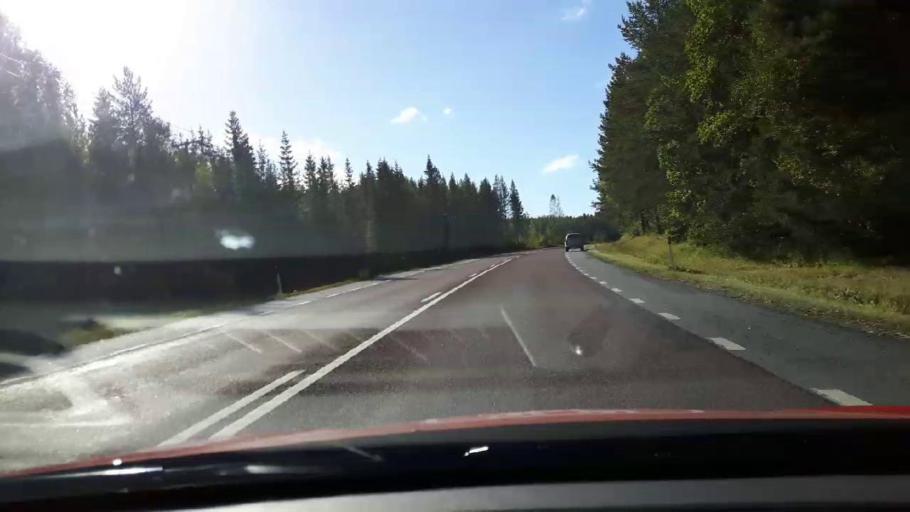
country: SE
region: Jaemtland
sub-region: Braecke Kommun
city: Braecke
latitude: 62.8066
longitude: 15.3682
